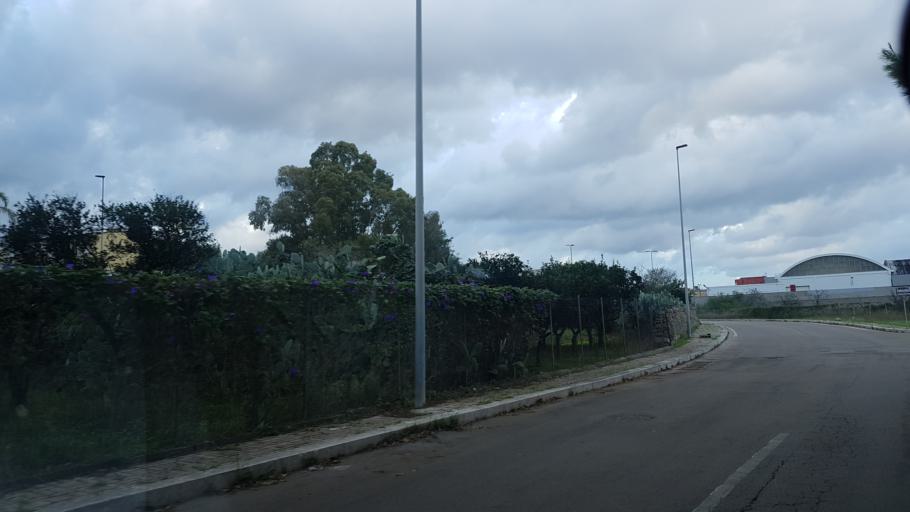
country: IT
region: Apulia
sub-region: Provincia di Brindisi
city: San Pietro Vernotico
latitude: 40.4902
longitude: 18.0018
